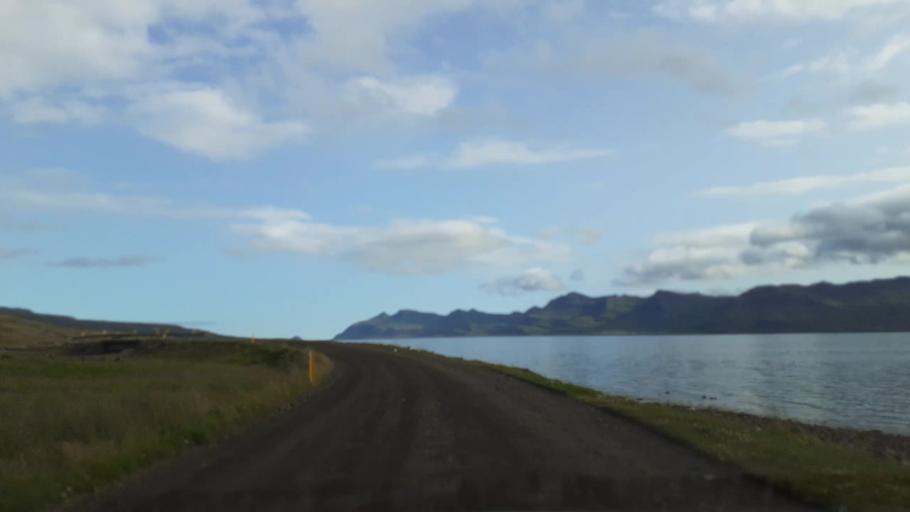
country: IS
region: East
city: Eskifjoerdur
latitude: 65.0359
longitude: -13.8745
